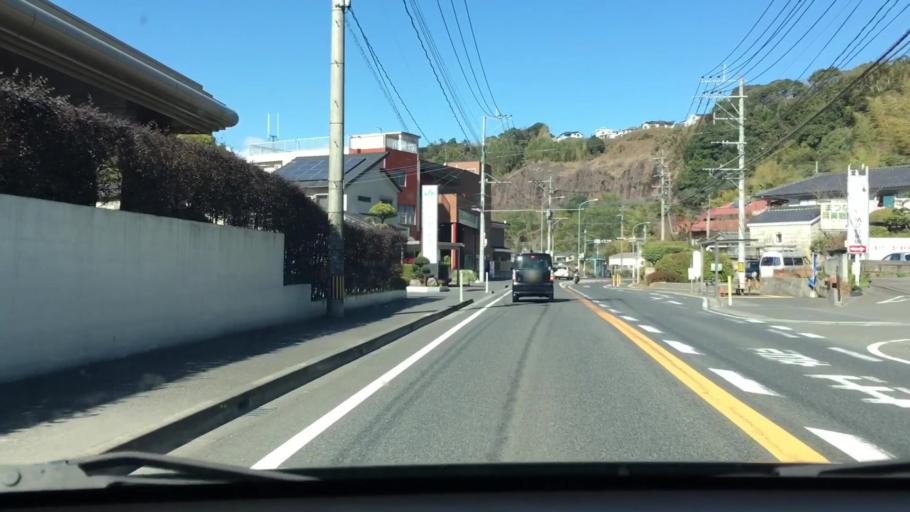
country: JP
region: Kagoshima
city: Kagoshima-shi
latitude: 31.6308
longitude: 130.5243
